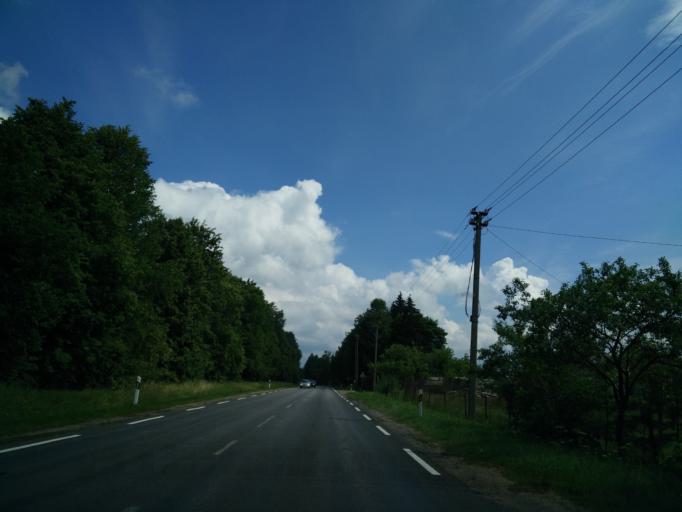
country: LT
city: Skaidiskes
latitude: 54.6921
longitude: 25.4617
